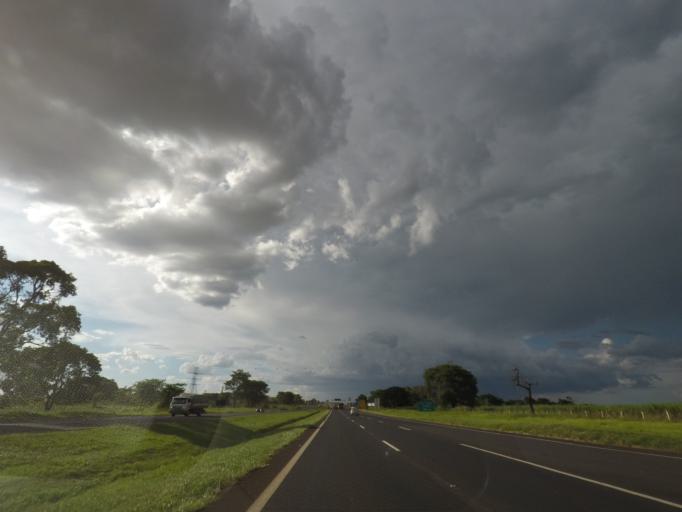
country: BR
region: Sao Paulo
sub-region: Ribeirao Preto
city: Ribeirao Preto
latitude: -21.1100
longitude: -47.7821
